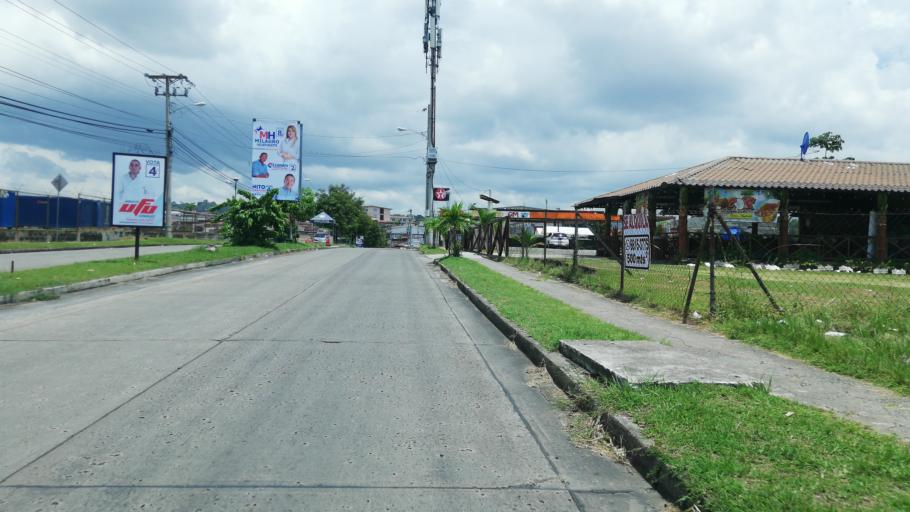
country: PA
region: Panama
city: San Miguelito
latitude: 9.0521
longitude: -79.4544
